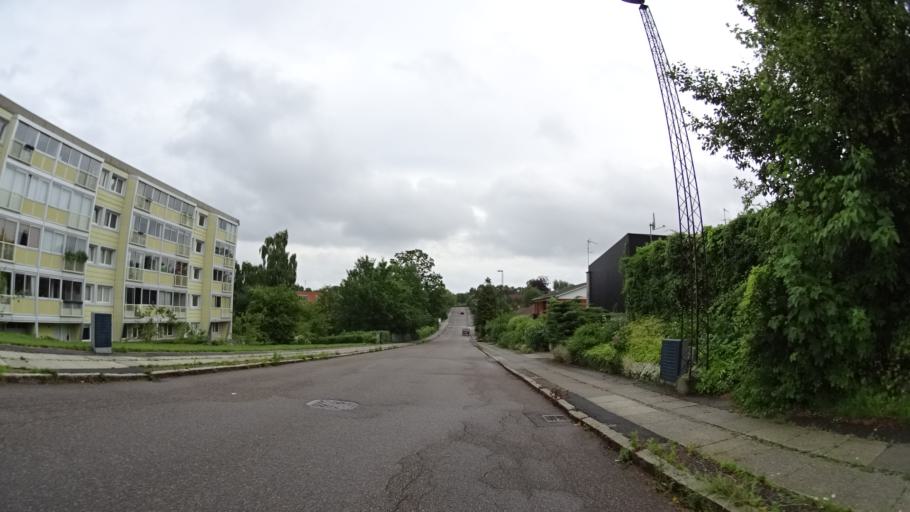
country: DK
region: Central Jutland
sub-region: Arhus Kommune
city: Arhus
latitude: 56.1284
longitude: 10.1783
